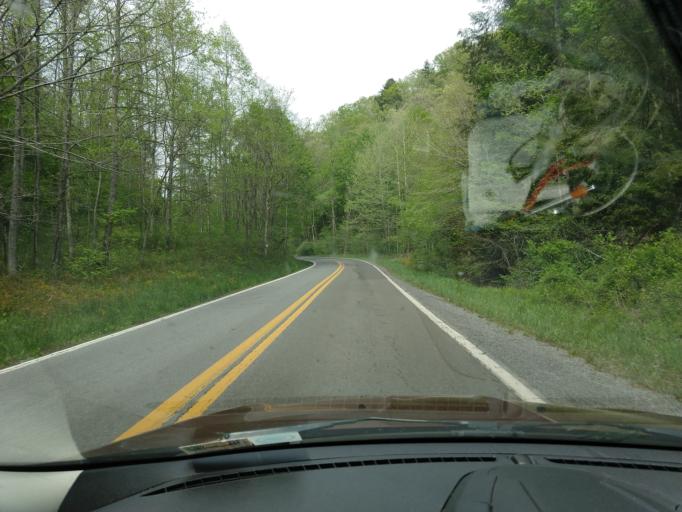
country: US
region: West Virginia
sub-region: McDowell County
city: Welch
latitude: 37.3454
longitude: -81.6688
